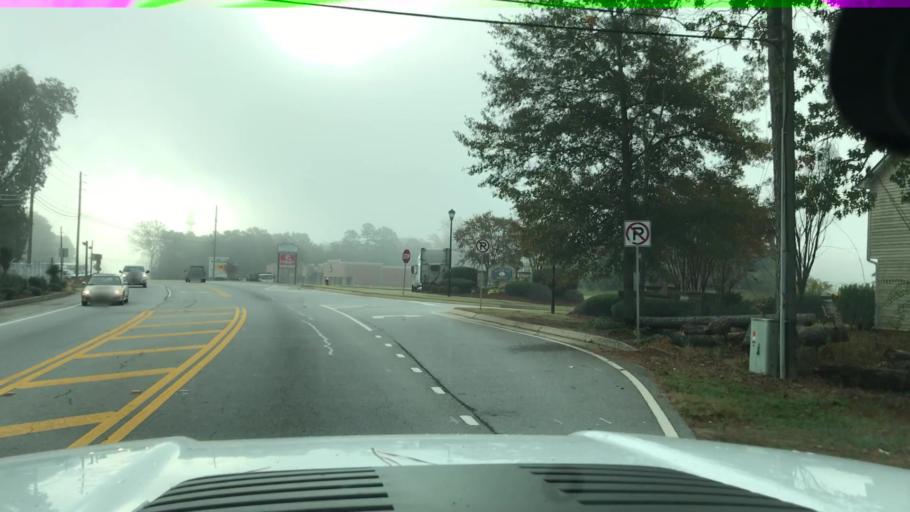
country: US
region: Georgia
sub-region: Barrow County
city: Russell
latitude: 33.9792
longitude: -83.7084
